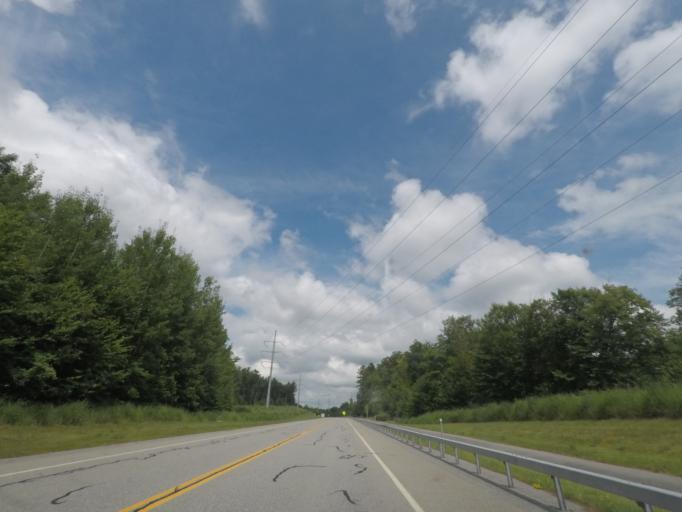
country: US
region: New York
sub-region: Saratoga County
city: Country Knolls
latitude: 42.9605
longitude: -73.7676
